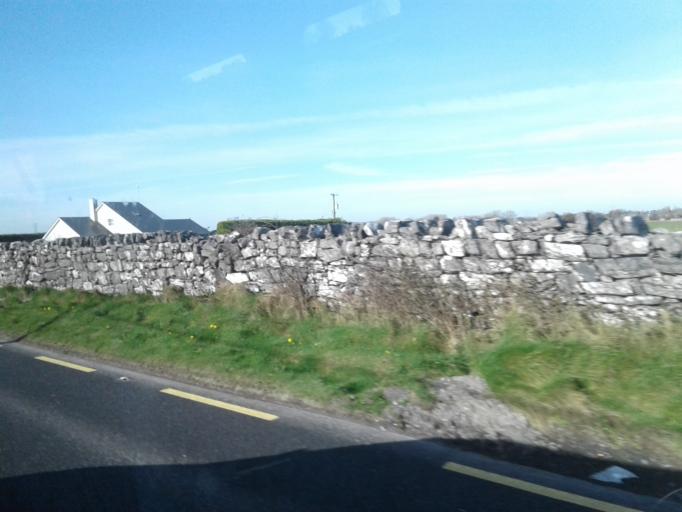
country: IE
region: Connaught
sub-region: County Galway
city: Oranmore
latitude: 53.1918
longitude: -8.8537
